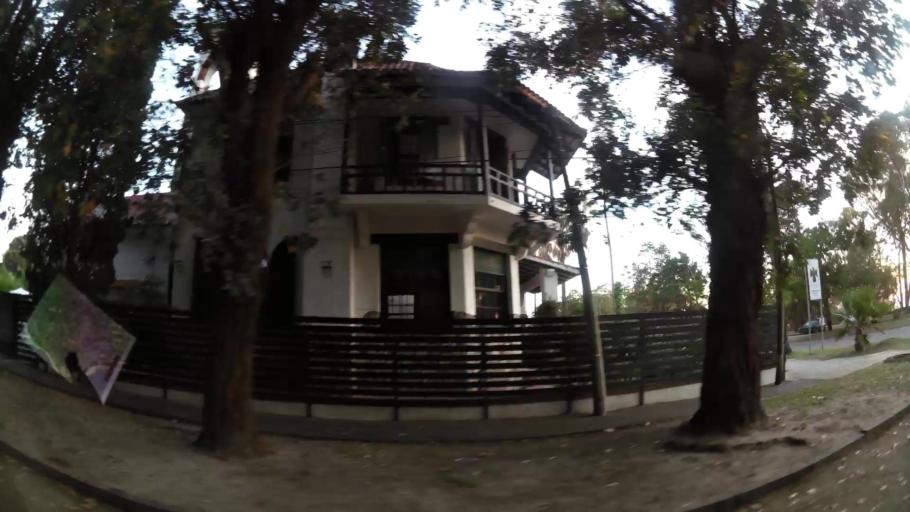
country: UY
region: Canelones
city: Atlantida
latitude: -34.7761
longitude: -55.7619
